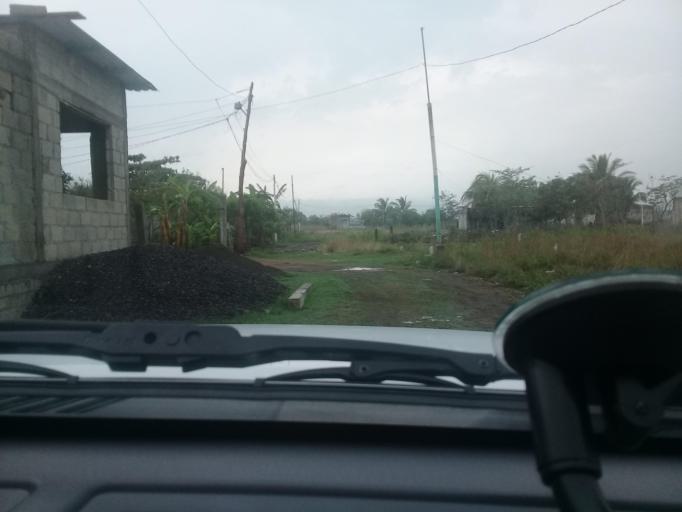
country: MX
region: Veracruz
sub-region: La Antigua
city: Nicolas Blanco (San Pancho)
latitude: 19.3568
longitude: -96.3515
